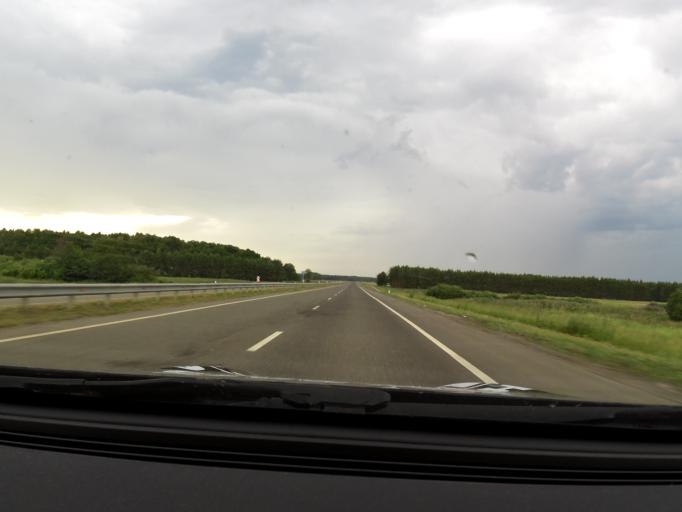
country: RU
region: Bashkortostan
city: Kushnarenkovo
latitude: 55.0606
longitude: 55.4109
